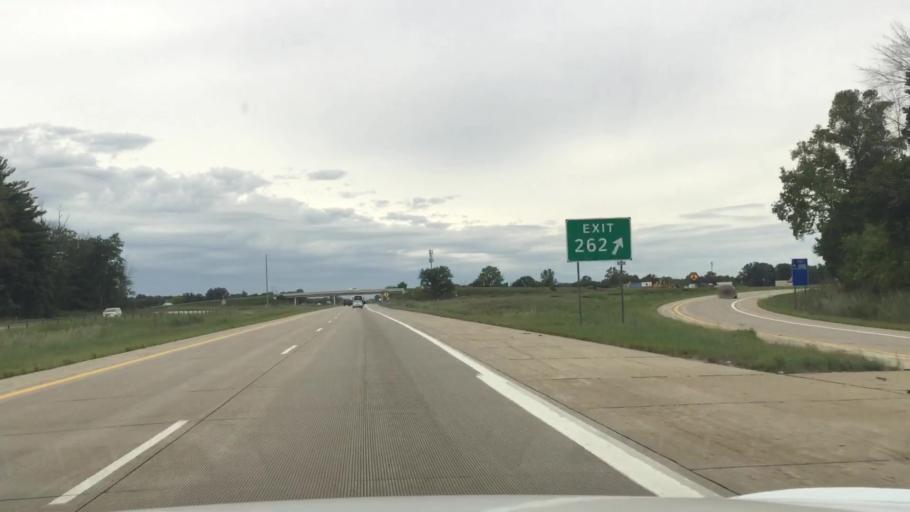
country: US
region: Michigan
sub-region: Saint Clair County
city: Saint Clair
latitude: 42.8659
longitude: -82.5542
